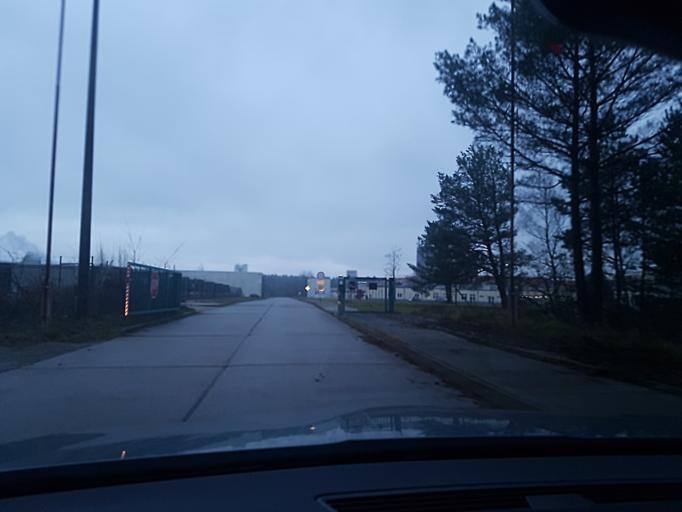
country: DE
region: Brandenburg
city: Schonewalde
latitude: 51.6332
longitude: 13.6310
